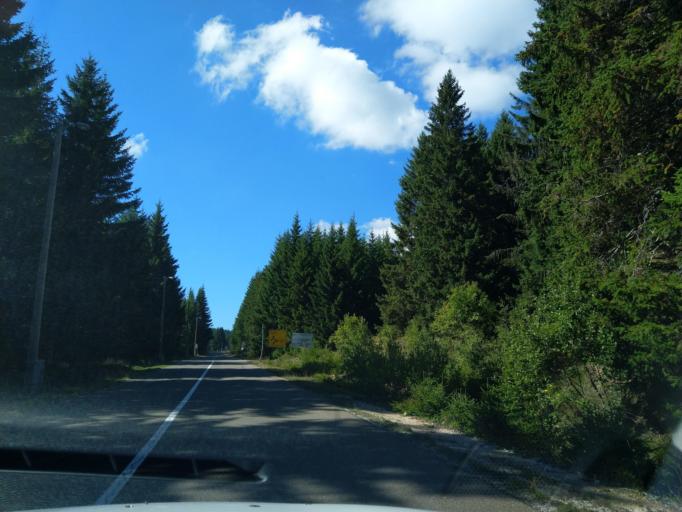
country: RS
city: Sokolovica
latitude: 43.2755
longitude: 20.3478
